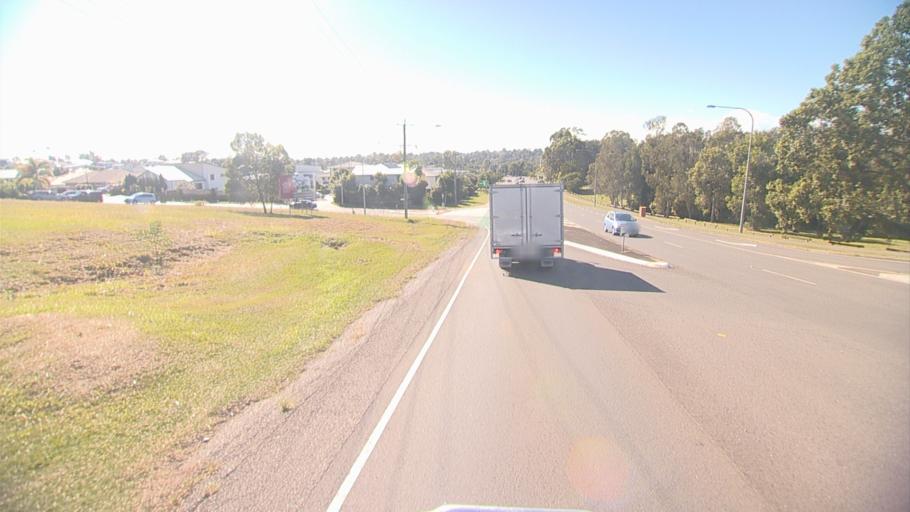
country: AU
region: Queensland
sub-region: Logan
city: Rochedale South
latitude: -27.6065
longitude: 153.1059
